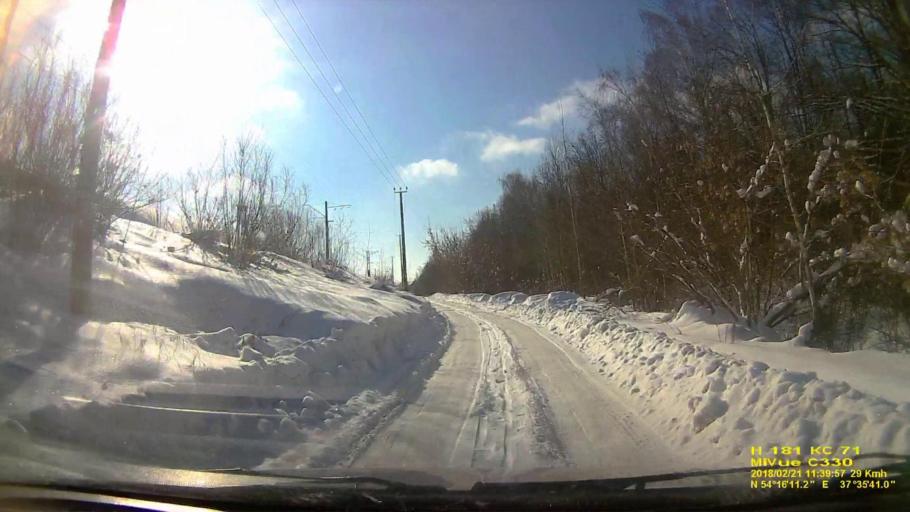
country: RU
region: Tula
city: Gorelki
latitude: 54.2697
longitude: 37.5947
